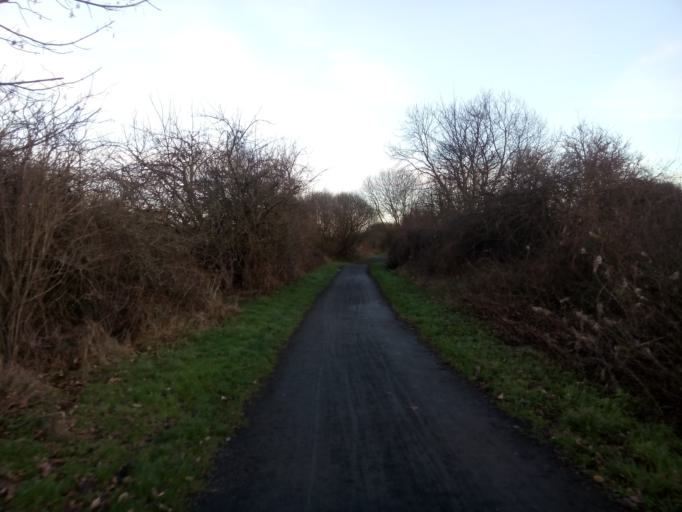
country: GB
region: England
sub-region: County Durham
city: Ushaw Moor
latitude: 54.7742
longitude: -1.6437
